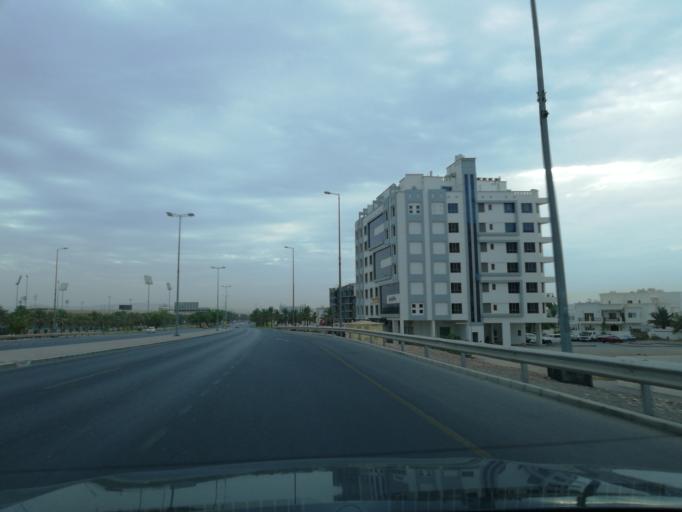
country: OM
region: Muhafazat Masqat
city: Bawshar
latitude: 23.5769
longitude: 58.4065
